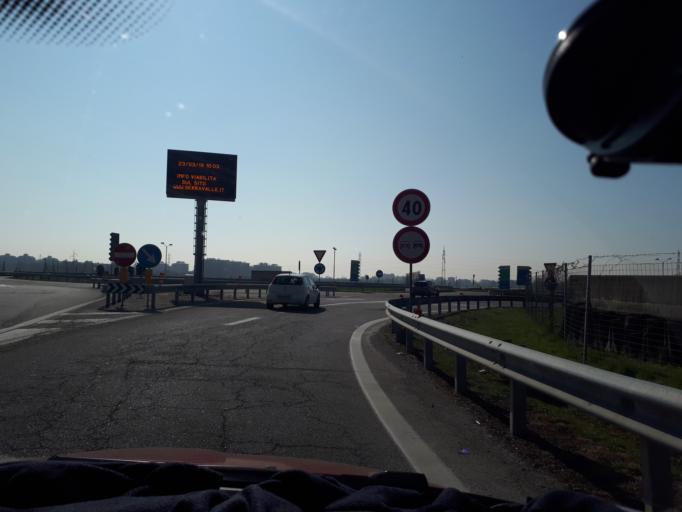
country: IT
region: Lombardy
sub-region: Citta metropolitana di Milano
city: Cusano Milanino
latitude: 45.5670
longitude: 9.1926
